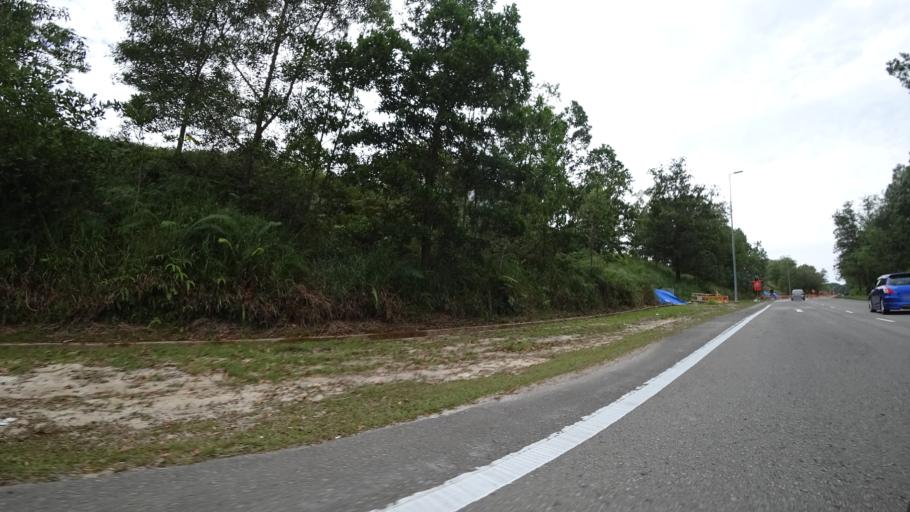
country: BN
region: Brunei and Muara
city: Bandar Seri Begawan
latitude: 4.9009
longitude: 114.8740
